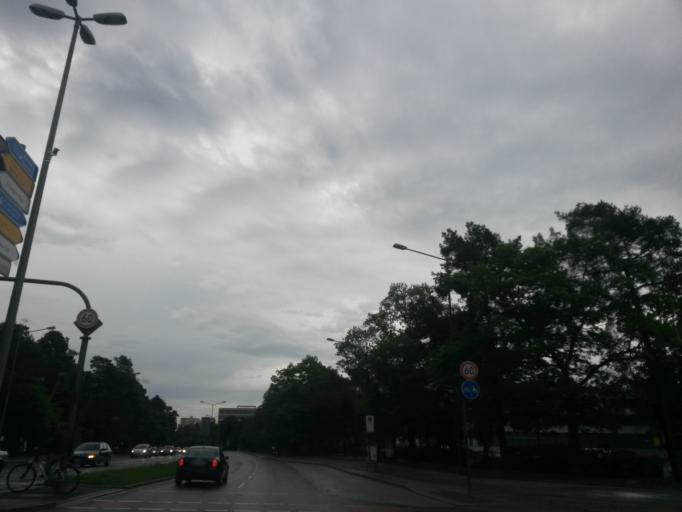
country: DE
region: Bavaria
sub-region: Regierungsbezirk Mittelfranken
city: Erlangen
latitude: 49.5775
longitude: 11.0041
